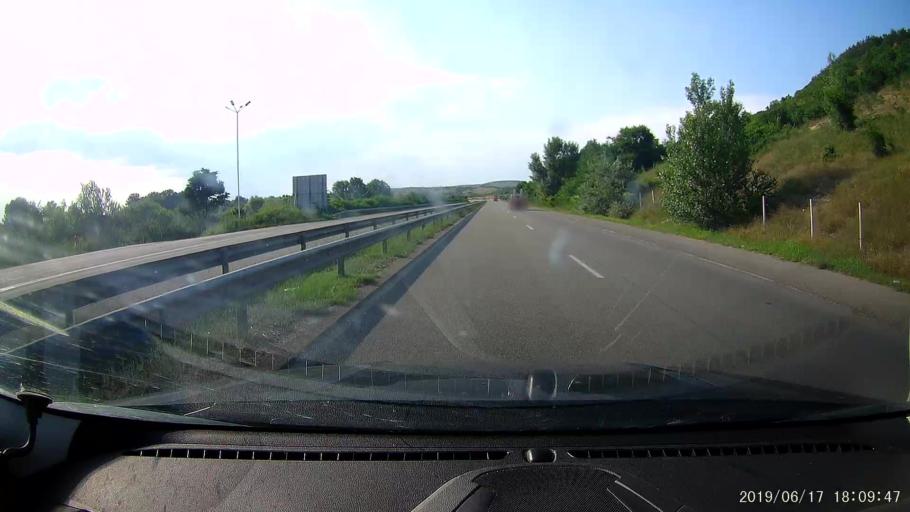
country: BG
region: Khaskovo
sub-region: Obshtina Lyubimets
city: Lyubimets
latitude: 41.8649
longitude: 26.0863
